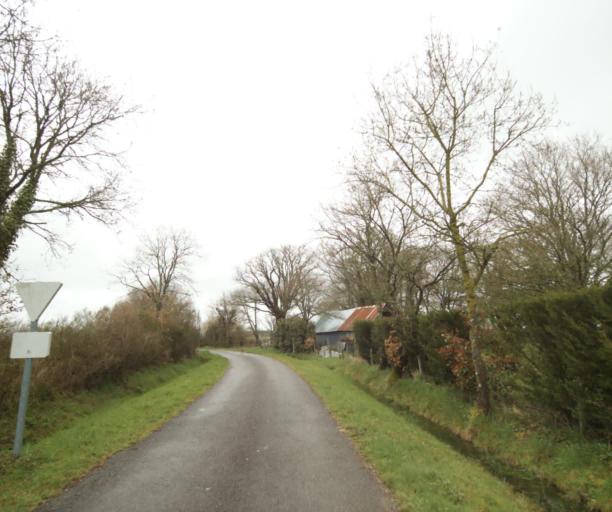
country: FR
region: Pays de la Loire
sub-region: Departement de la Loire-Atlantique
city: Quilly
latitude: 47.4561
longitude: -1.9004
